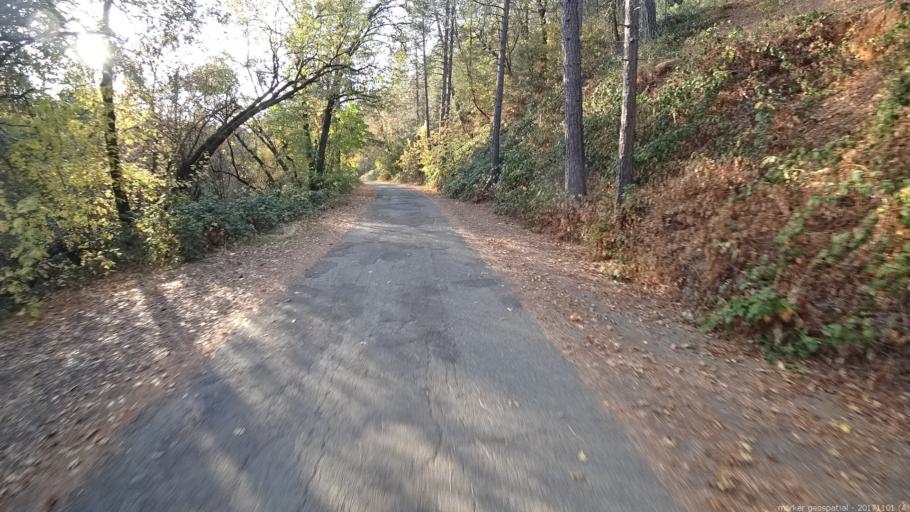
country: US
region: California
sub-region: Shasta County
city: Shasta Lake
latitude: 40.8163
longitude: -122.3294
